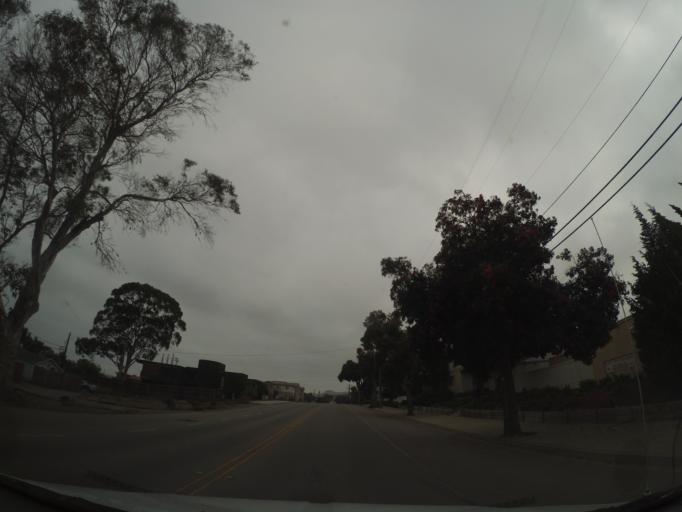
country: US
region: California
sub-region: San Luis Obispo County
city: Morro Bay
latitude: 35.3623
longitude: -120.8500
